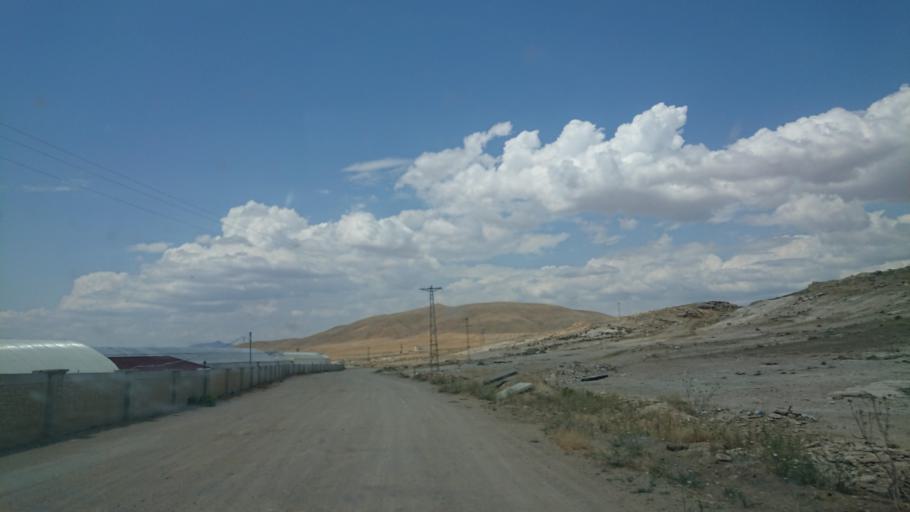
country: TR
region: Aksaray
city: Sariyahsi
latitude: 38.9995
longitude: 33.9122
